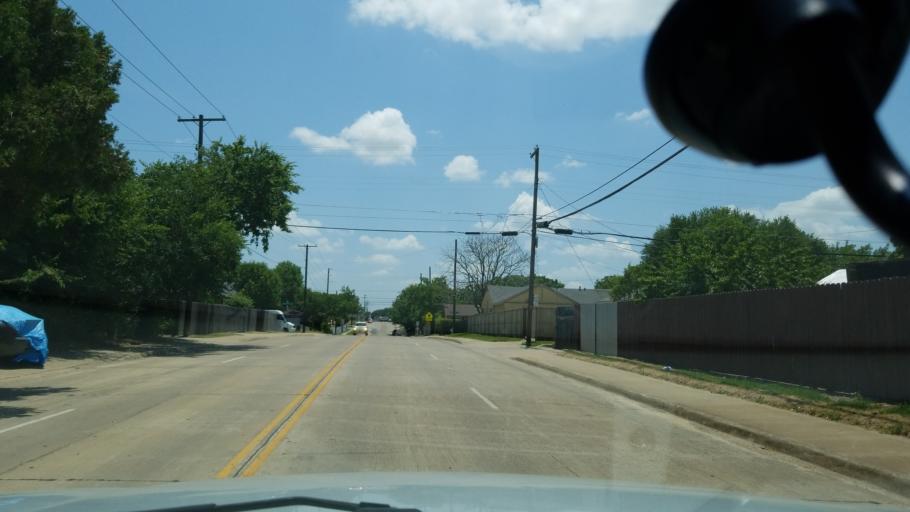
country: US
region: Texas
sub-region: Dallas County
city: Cockrell Hill
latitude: 32.7252
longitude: -96.8689
